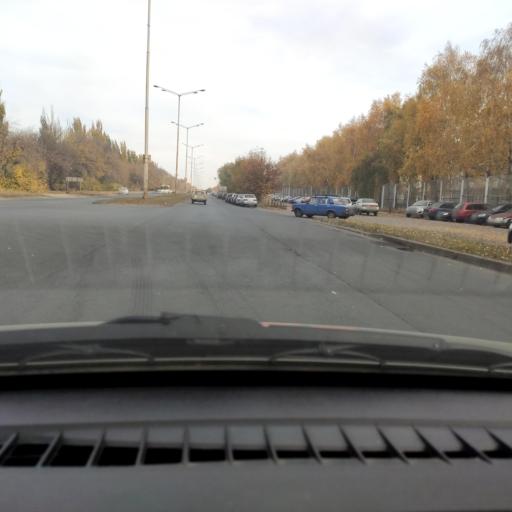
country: RU
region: Samara
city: Tol'yatti
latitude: 53.5699
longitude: 49.2530
